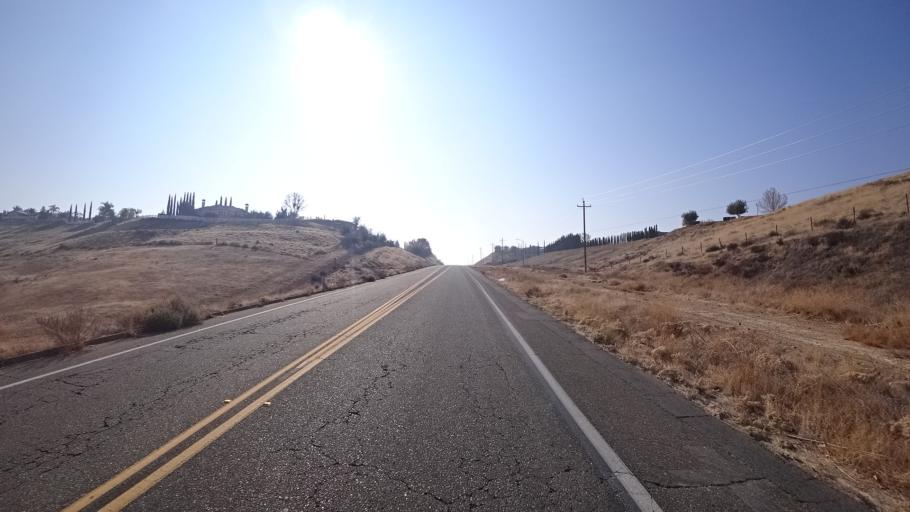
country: US
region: California
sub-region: Kern County
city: Oildale
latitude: 35.4189
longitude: -118.8581
